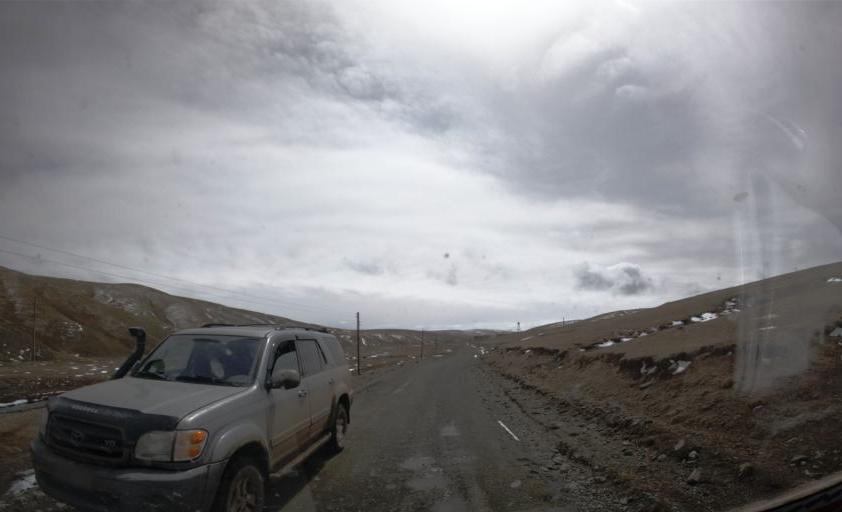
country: KG
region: Naryn
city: Naryn
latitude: 41.0740
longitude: 76.4458
